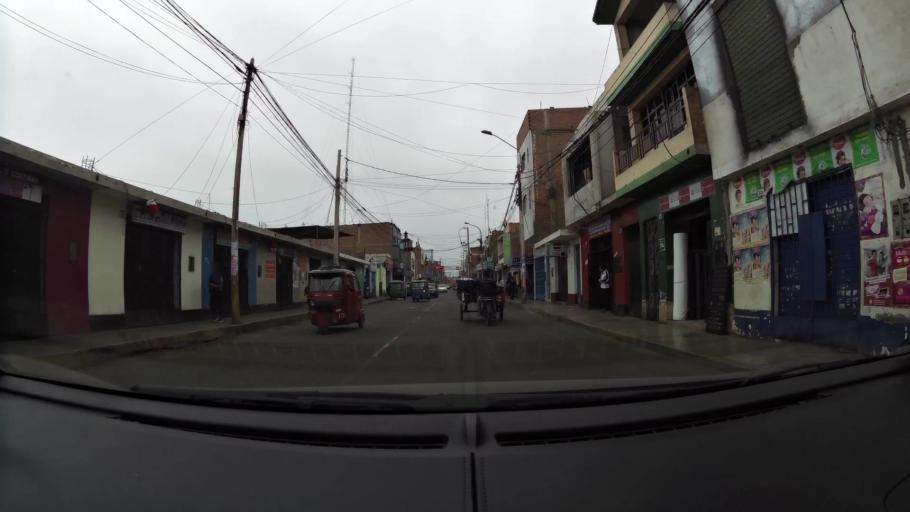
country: PE
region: Lima
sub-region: Barranca
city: Barranca
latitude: -10.7515
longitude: -77.7625
